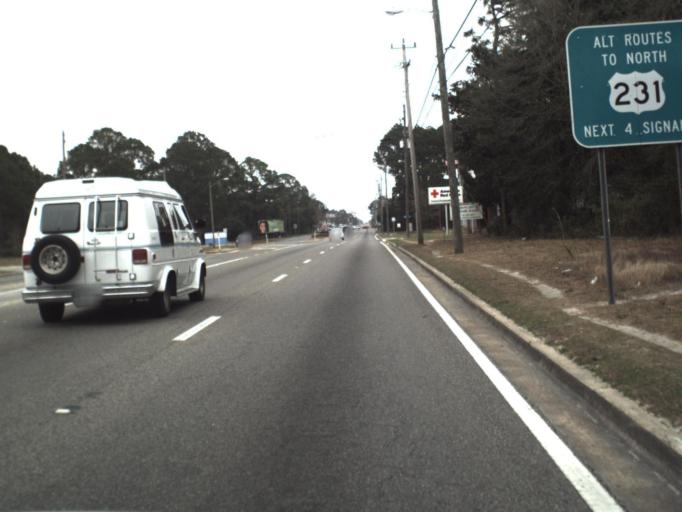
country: US
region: Florida
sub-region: Bay County
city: Panama City
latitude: 30.1750
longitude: -85.6550
